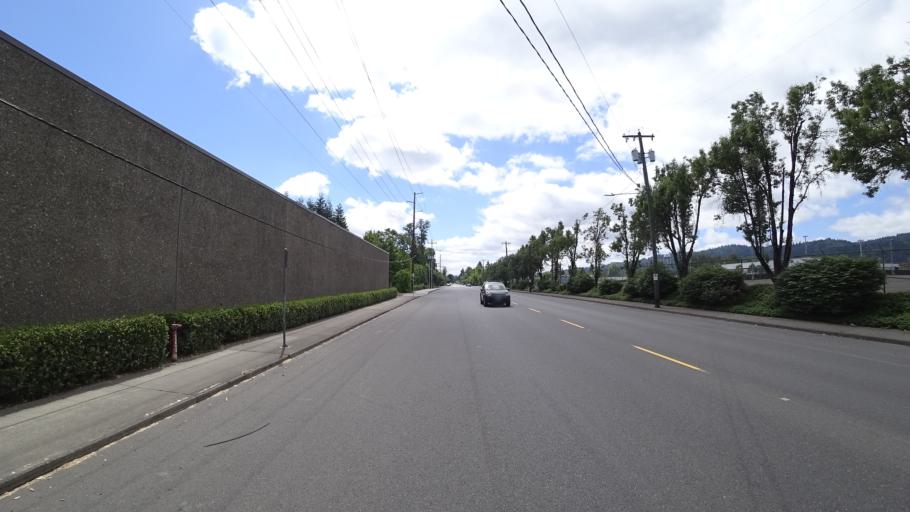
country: US
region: Oregon
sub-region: Washington County
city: West Haven
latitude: 45.6034
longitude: -122.7645
